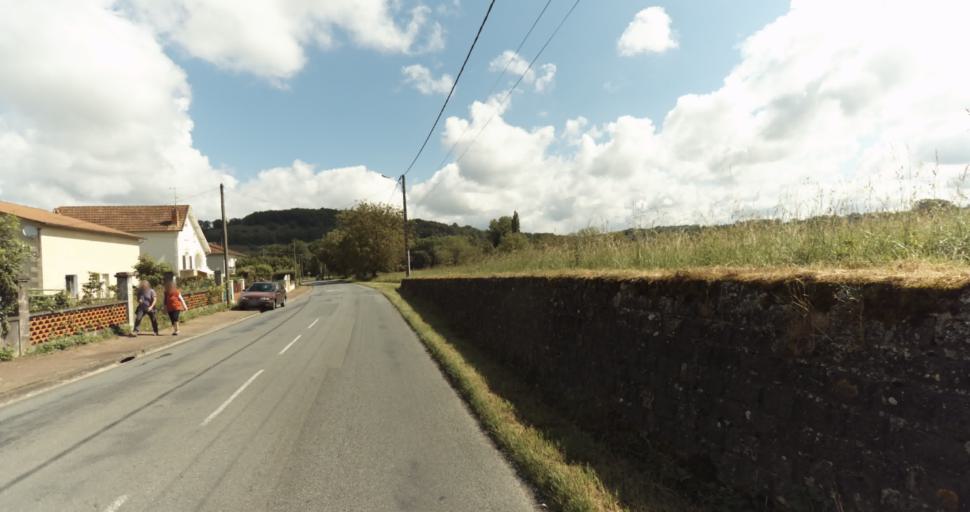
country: FR
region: Aquitaine
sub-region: Departement de la Dordogne
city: Le Bugue
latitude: 44.8507
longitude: 0.9101
